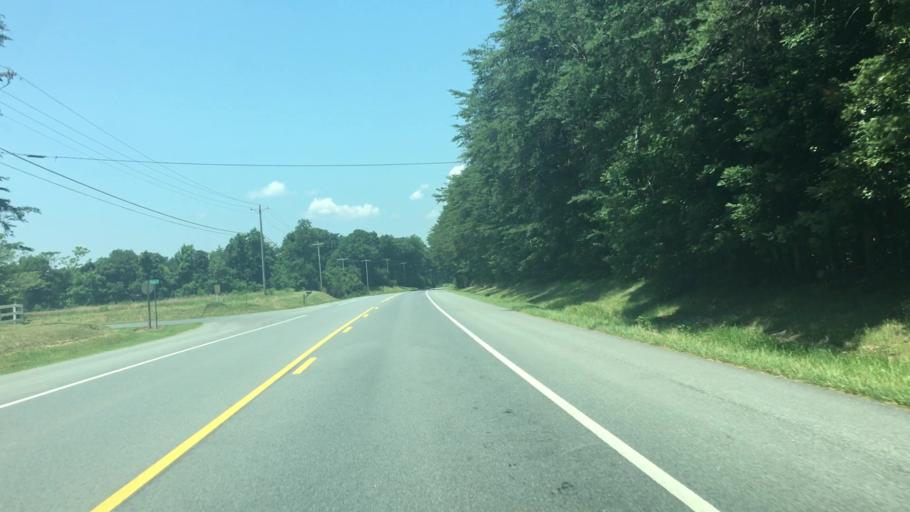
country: US
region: Maryland
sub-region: Saint Mary's County
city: Mechanicsville
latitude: 38.3757
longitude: -76.8128
